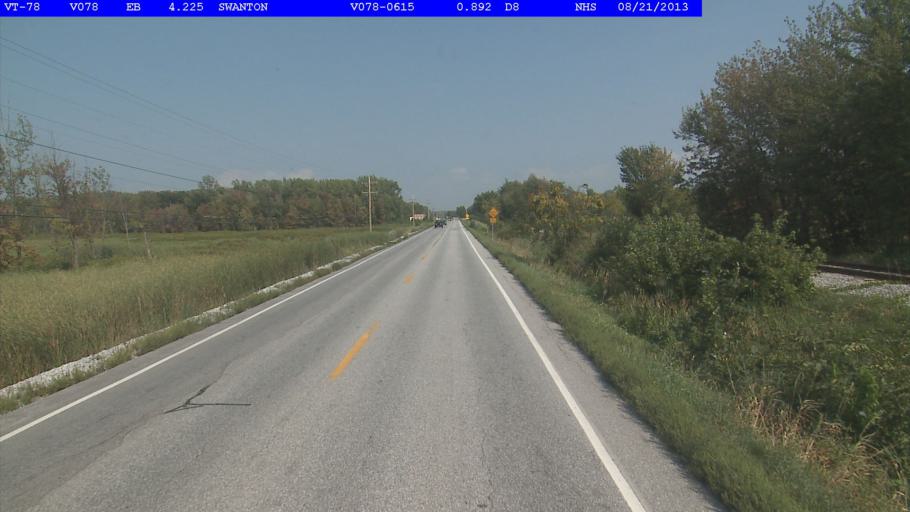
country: US
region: Vermont
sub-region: Franklin County
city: Swanton
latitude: 44.9696
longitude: -73.2031
